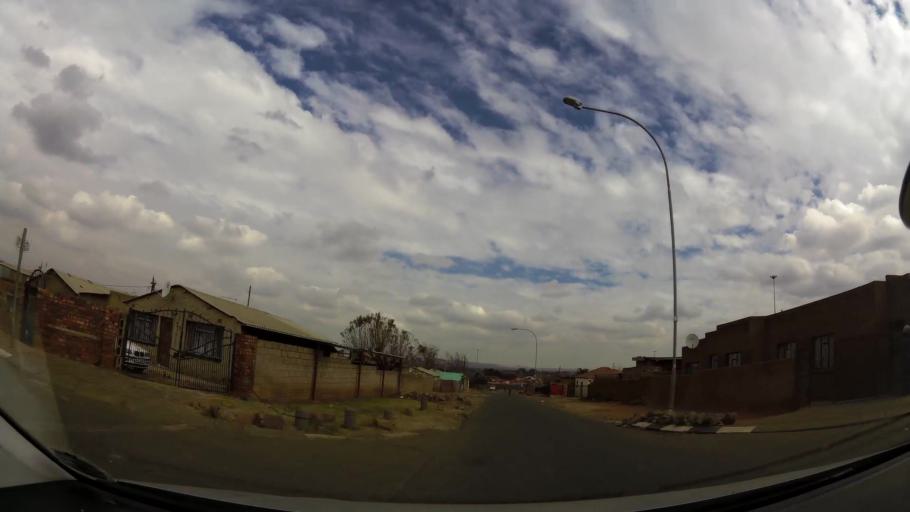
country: ZA
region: Gauteng
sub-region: City of Johannesburg Metropolitan Municipality
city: Soweto
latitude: -26.2784
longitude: 27.8500
